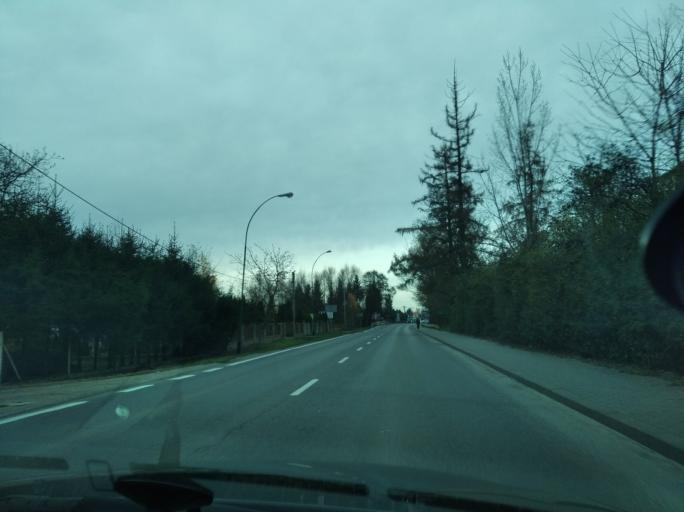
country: PL
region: Subcarpathian Voivodeship
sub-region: Powiat lancucki
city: Lancut
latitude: 50.0938
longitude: 22.2313
